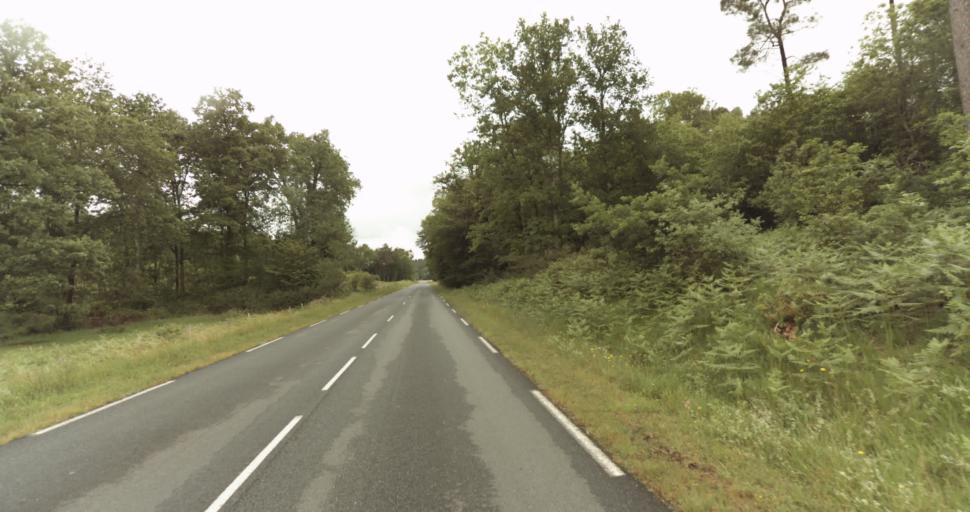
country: FR
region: Aquitaine
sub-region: Departement de la Dordogne
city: Belves
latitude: 44.6802
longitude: 0.9916
